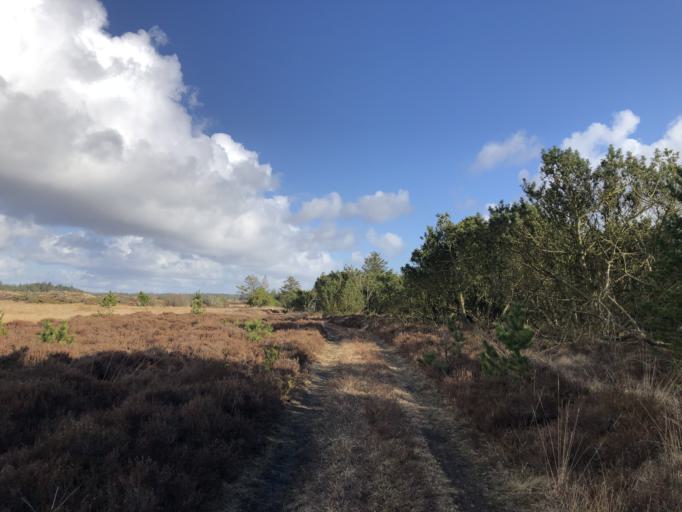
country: DK
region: Central Jutland
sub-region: Holstebro Kommune
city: Ulfborg
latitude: 56.2736
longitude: 8.3518
